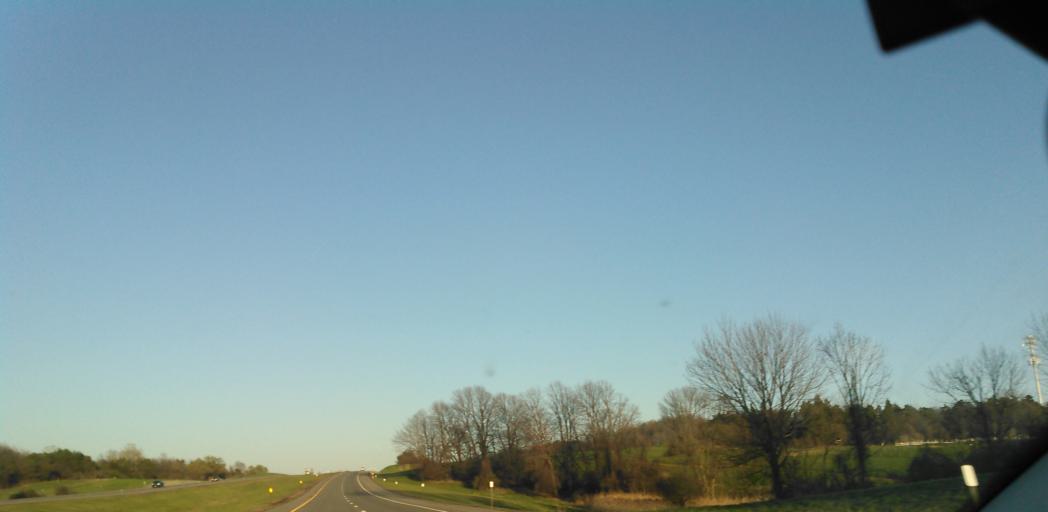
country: US
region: New York
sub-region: Monroe County
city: Pittsford
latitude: 43.0436
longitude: -77.5539
